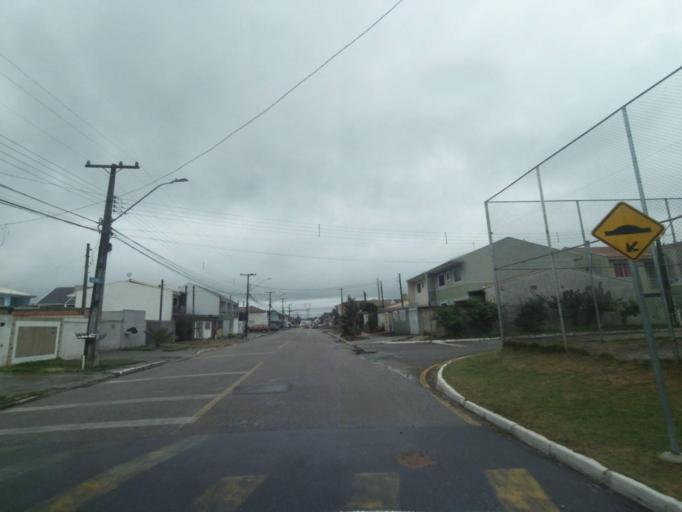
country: BR
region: Parana
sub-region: Araucaria
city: Araucaria
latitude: -25.5404
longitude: -49.3420
